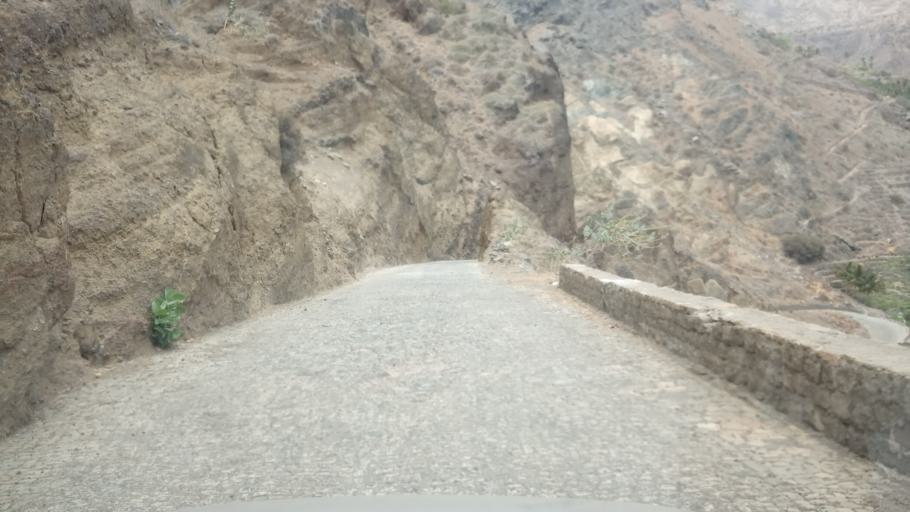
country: CV
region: Brava
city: Vila Nova Sintra
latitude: 14.8752
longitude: -24.7325
